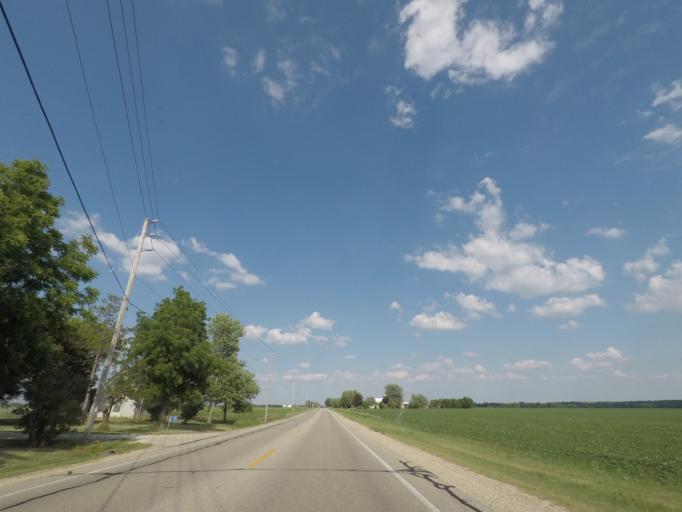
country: US
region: Wisconsin
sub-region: Walworth County
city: East Troy
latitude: 42.7928
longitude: -88.4643
